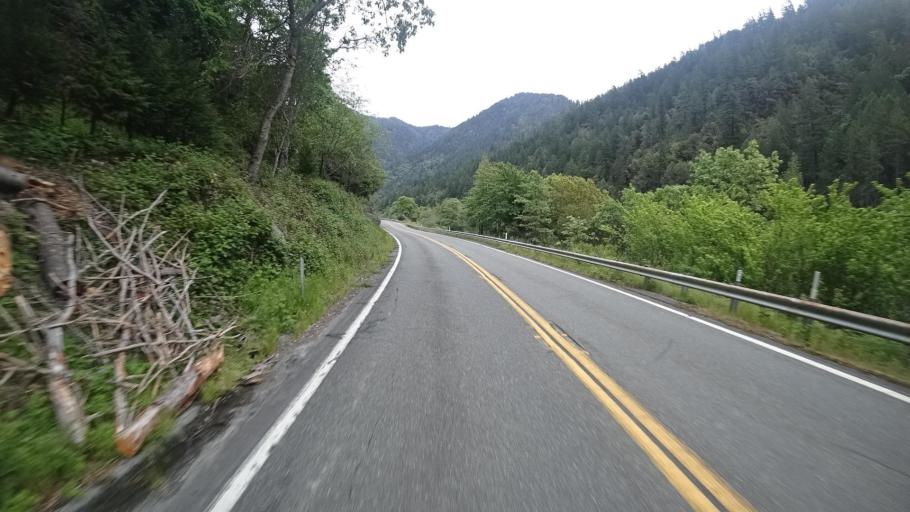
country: US
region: California
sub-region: Humboldt County
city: Willow Creek
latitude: 41.2099
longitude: -123.6571
